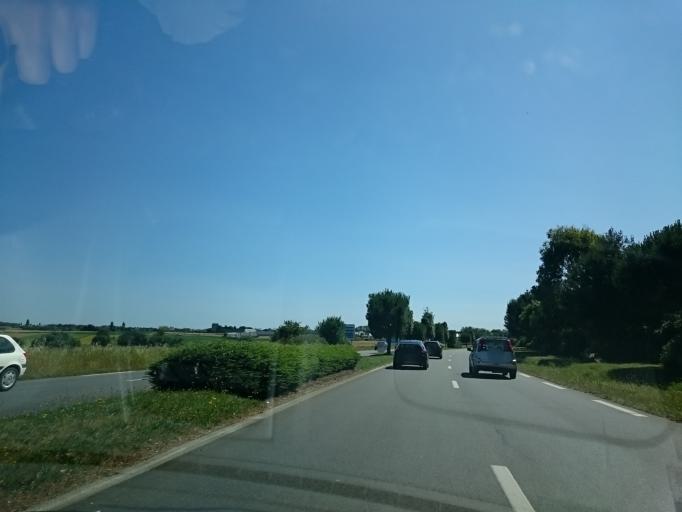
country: FR
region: Brittany
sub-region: Departement d'Ille-et-Vilaine
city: Saint-Malo
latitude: 48.6544
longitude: -1.9679
